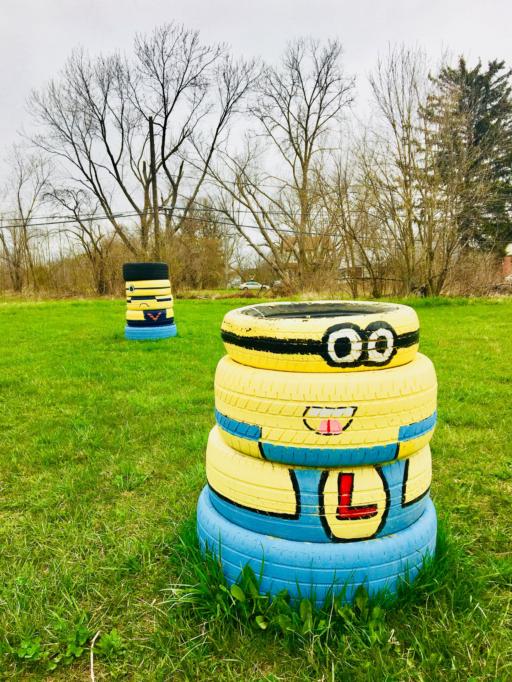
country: US
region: Michigan
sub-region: Macomb County
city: Eastpointe
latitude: 42.4232
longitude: -82.9740
